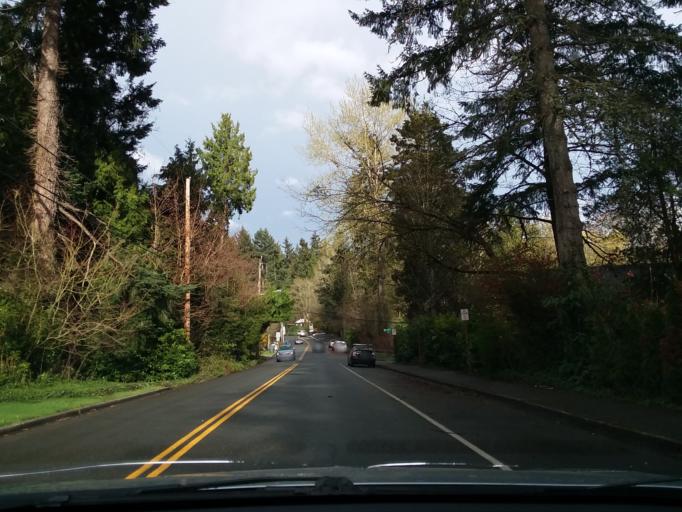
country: US
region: Washington
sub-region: King County
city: Lake Forest Park
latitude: 47.7563
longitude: -122.2830
